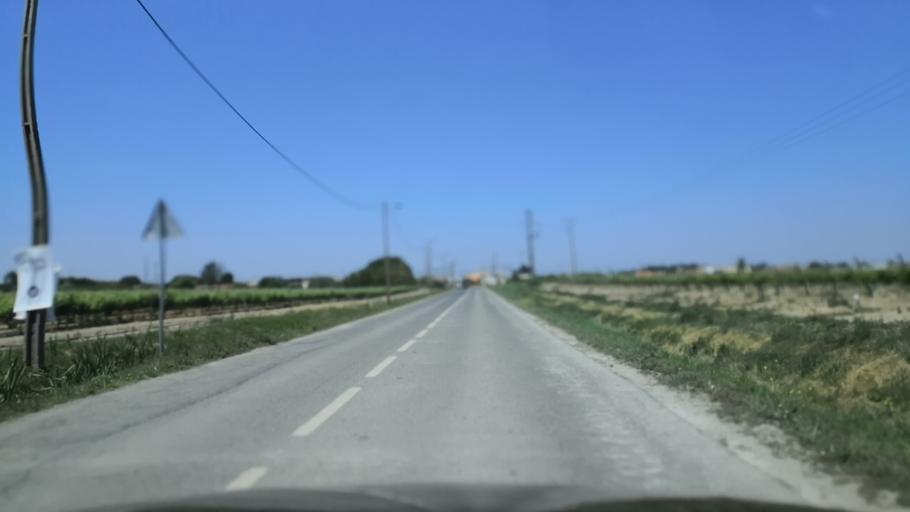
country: PT
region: Setubal
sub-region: Palmela
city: Pinhal Novo
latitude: 38.6361
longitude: -8.7421
